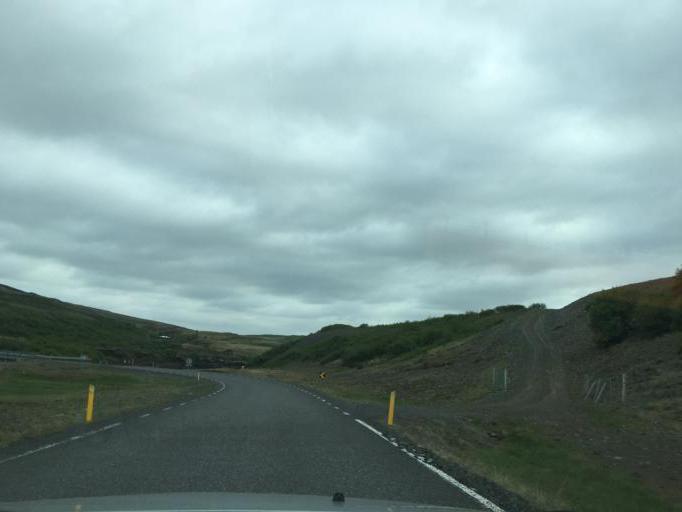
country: IS
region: South
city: Vestmannaeyjar
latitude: 64.2628
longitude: -20.2247
